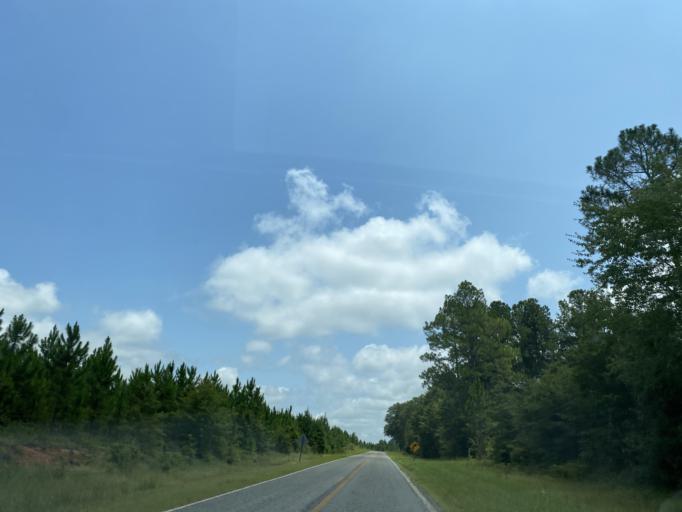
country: US
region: Georgia
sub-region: Wheeler County
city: Alamo
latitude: 32.0791
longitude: -82.7448
